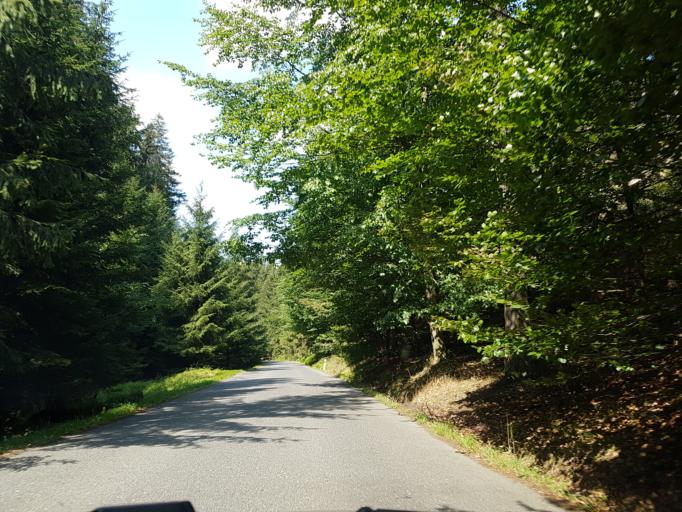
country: CZ
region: Ustecky
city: Mikulasovice
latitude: 50.8644
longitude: 14.3362
